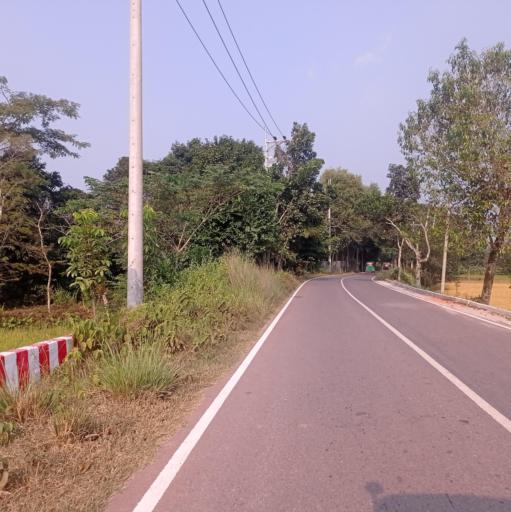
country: BD
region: Dhaka
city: Bhairab Bazar
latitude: 24.0733
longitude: 90.8448
